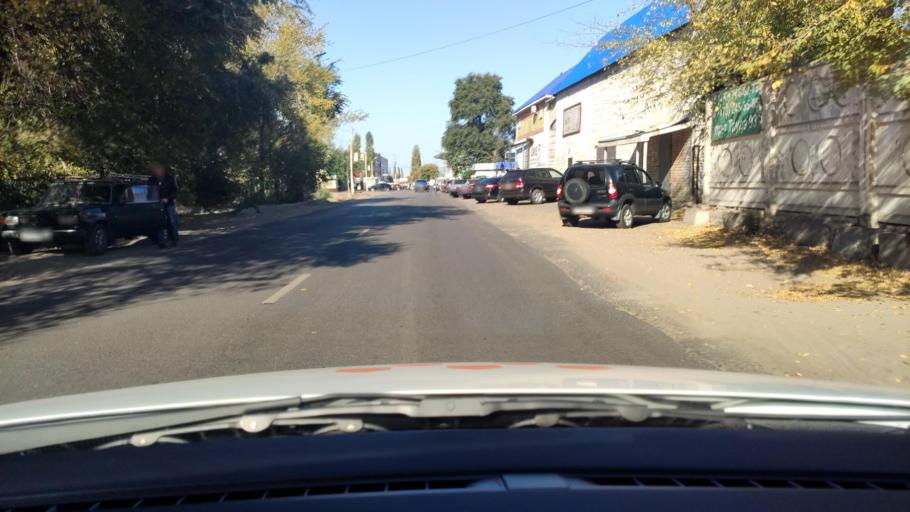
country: RU
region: Voronezj
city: Maslovka
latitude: 51.5967
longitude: 39.2490
